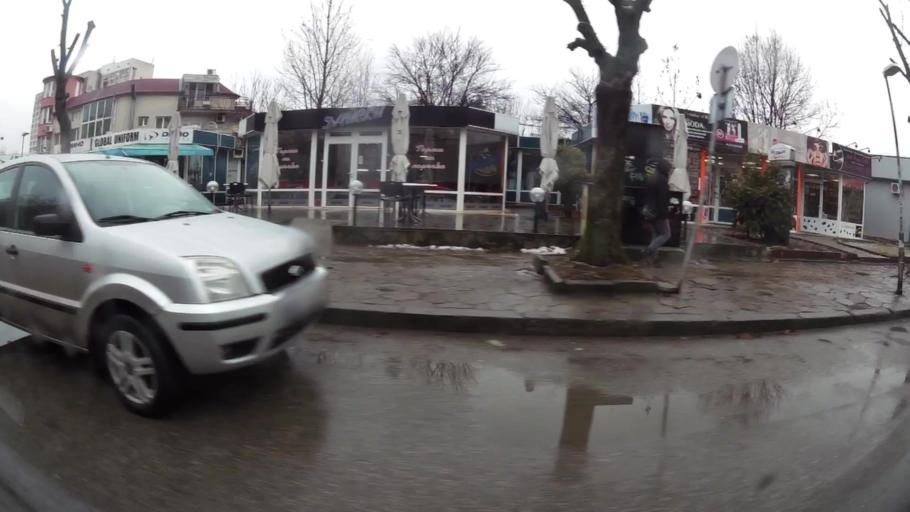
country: BG
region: Sofia-Capital
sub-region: Stolichna Obshtina
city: Sofia
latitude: 42.6685
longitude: 23.3962
